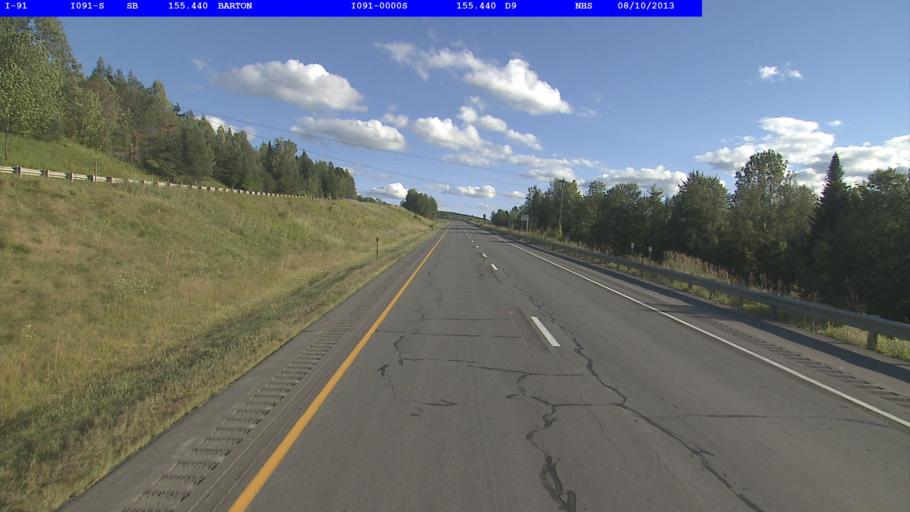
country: US
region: Vermont
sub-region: Orleans County
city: Newport
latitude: 44.7289
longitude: -72.1804
